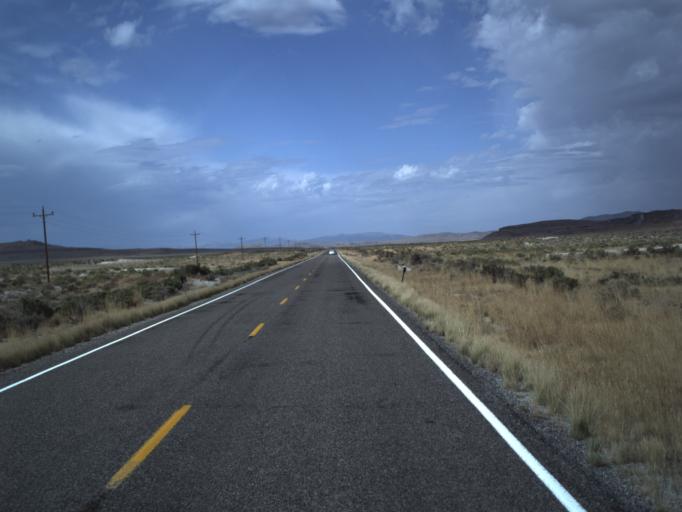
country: US
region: Utah
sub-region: Tooele County
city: Wendover
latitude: 41.4252
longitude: -113.8545
